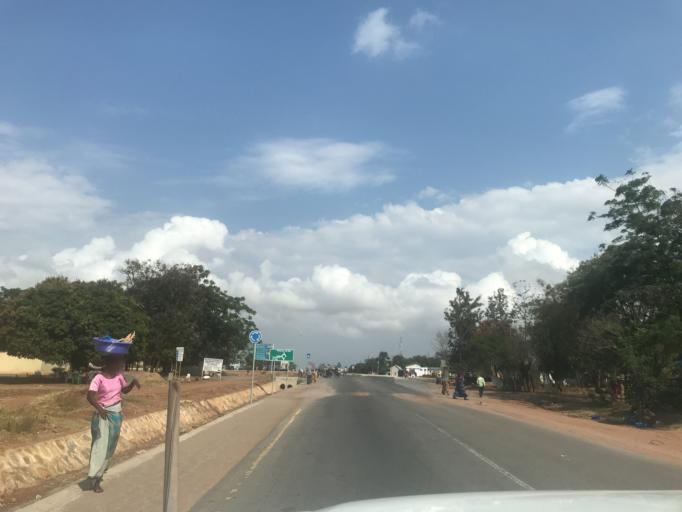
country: TZ
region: Mwanza
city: Usagara
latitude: -2.5555
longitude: 33.0511
